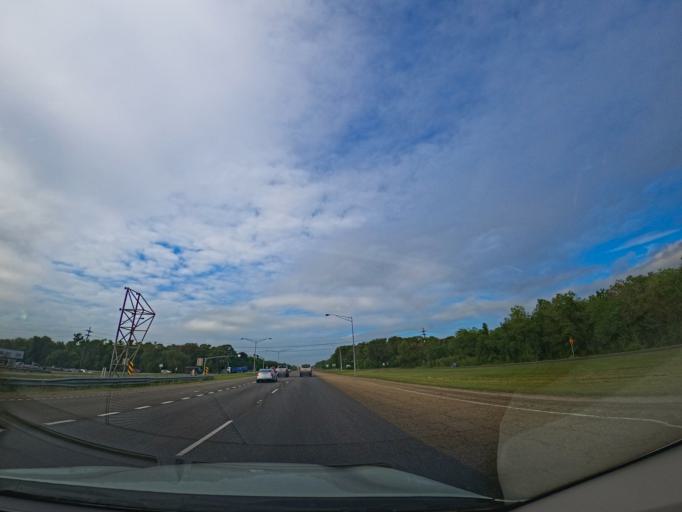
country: US
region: Louisiana
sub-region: Saint Mary Parish
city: Berwick
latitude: 29.6908
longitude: -91.2299
